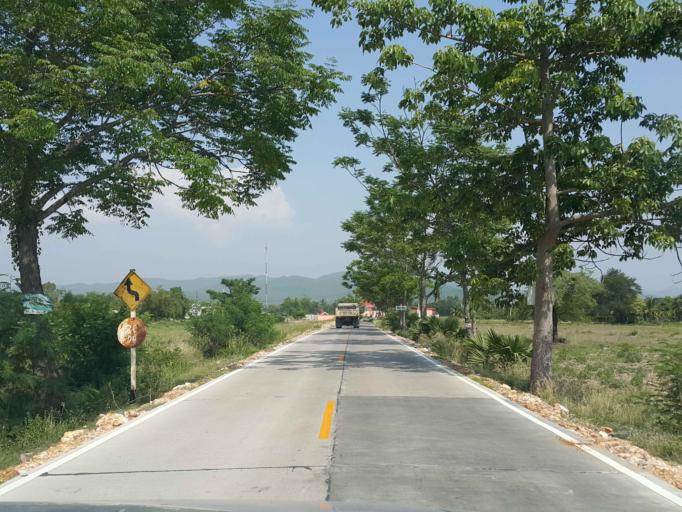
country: TH
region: Chiang Mai
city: San Kamphaeng
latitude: 18.7894
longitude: 99.1552
